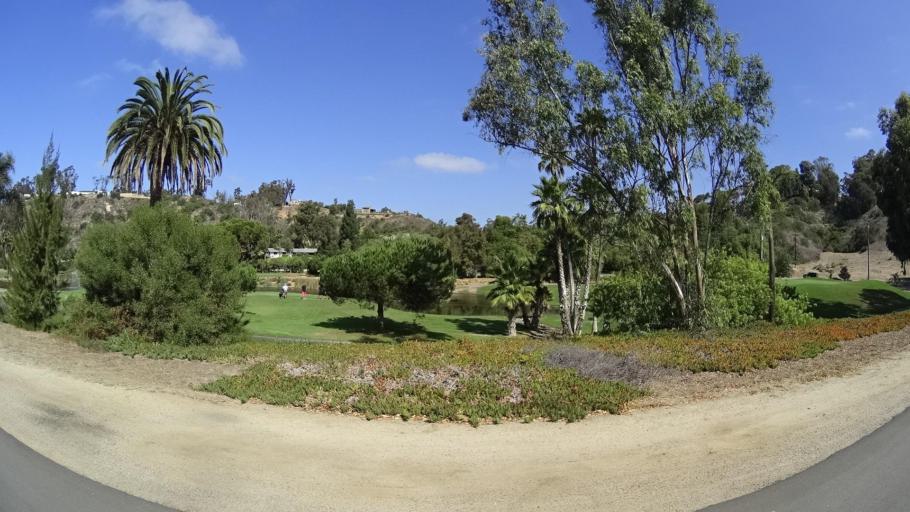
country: US
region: California
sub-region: San Diego County
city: Fairbanks Ranch
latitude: 32.9943
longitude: -117.2123
